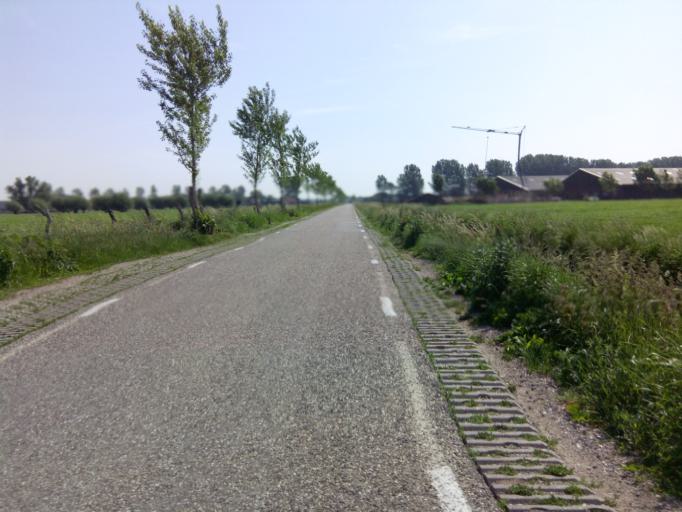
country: NL
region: Utrecht
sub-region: Gemeente Utrechtse Heuvelrug
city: Leersum
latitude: 51.9874
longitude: 5.3922
